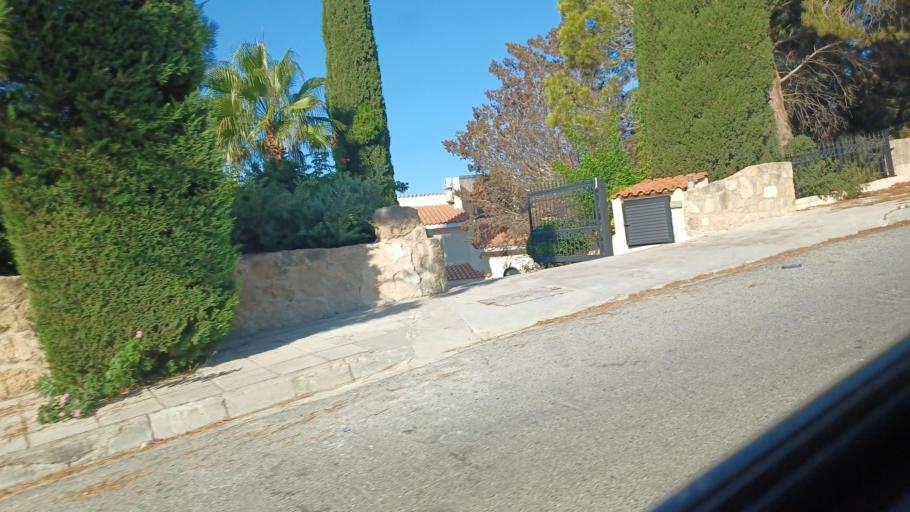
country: CY
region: Pafos
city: Tala
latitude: 34.8441
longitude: 32.4386
